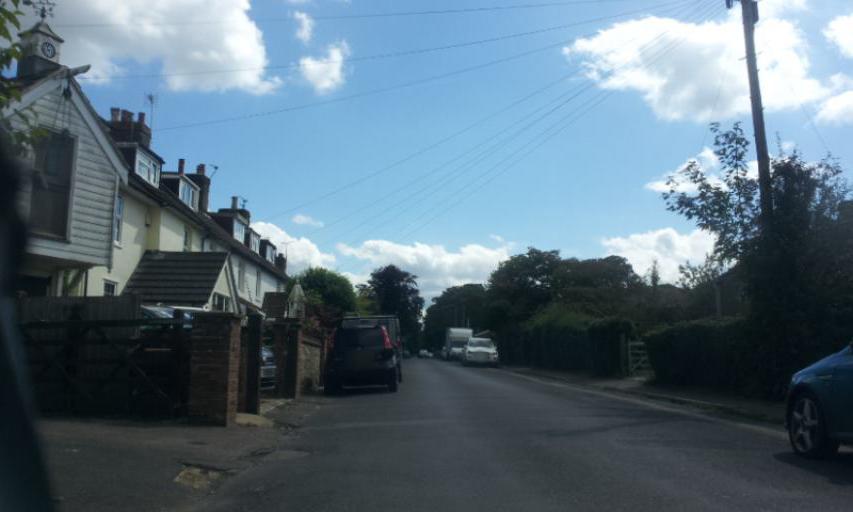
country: GB
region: England
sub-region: Kent
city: Maidstone
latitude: 51.2313
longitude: 0.5320
